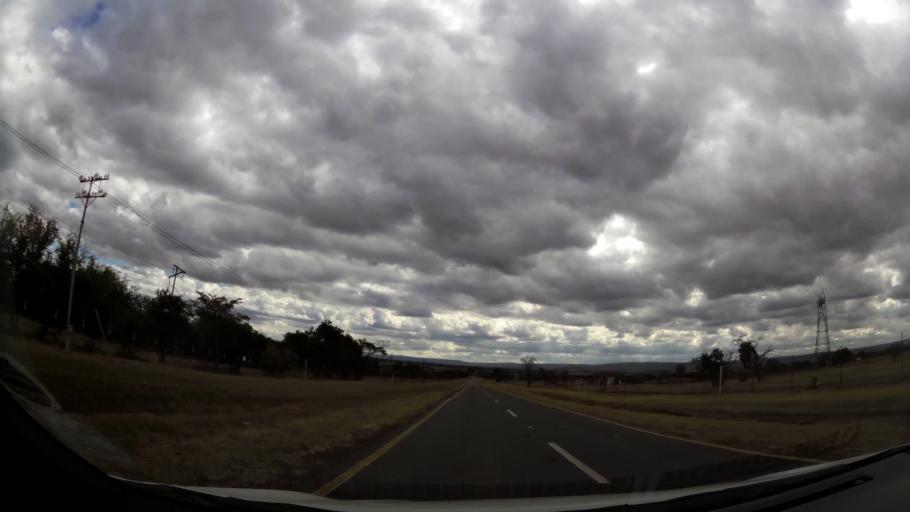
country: ZA
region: Limpopo
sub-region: Waterberg District Municipality
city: Modimolle
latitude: -24.7592
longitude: 28.4550
